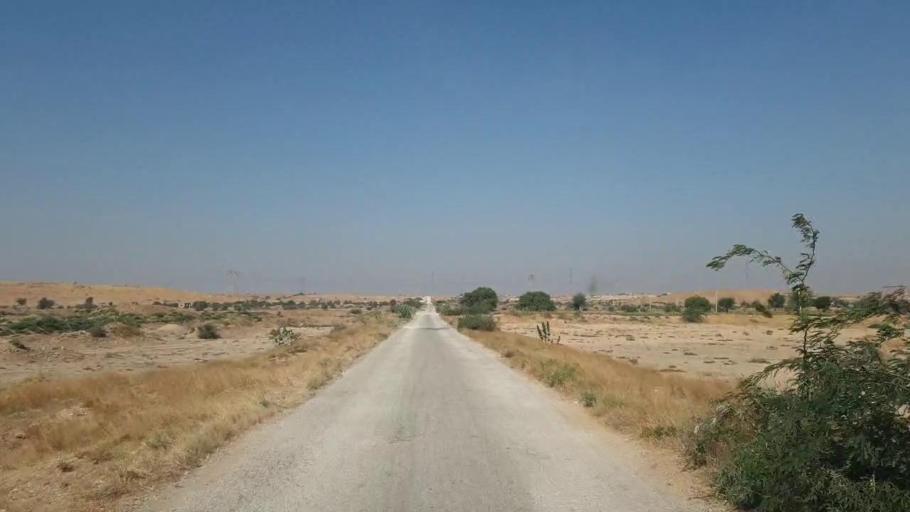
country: PK
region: Sindh
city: Thatta
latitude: 25.1908
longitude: 67.8029
